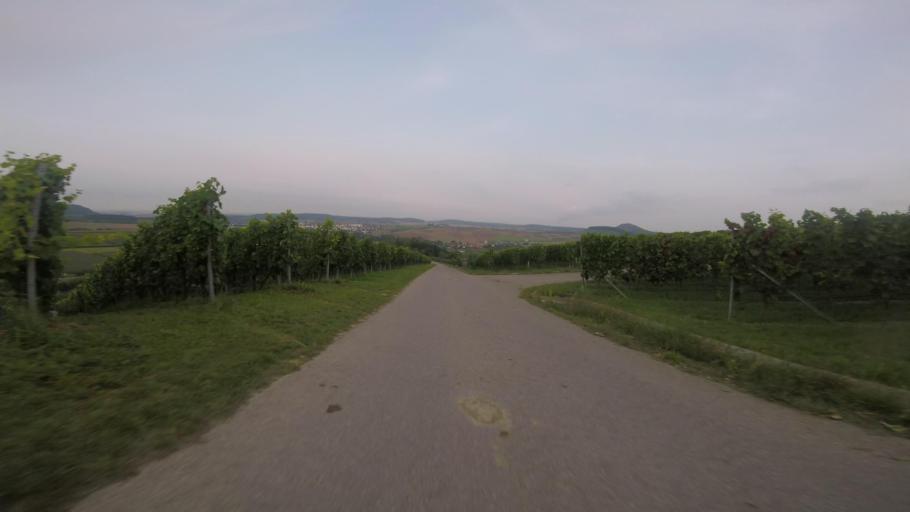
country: DE
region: Baden-Wuerttemberg
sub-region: Regierungsbezirk Stuttgart
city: Oberstenfeld
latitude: 49.0126
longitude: 9.3252
